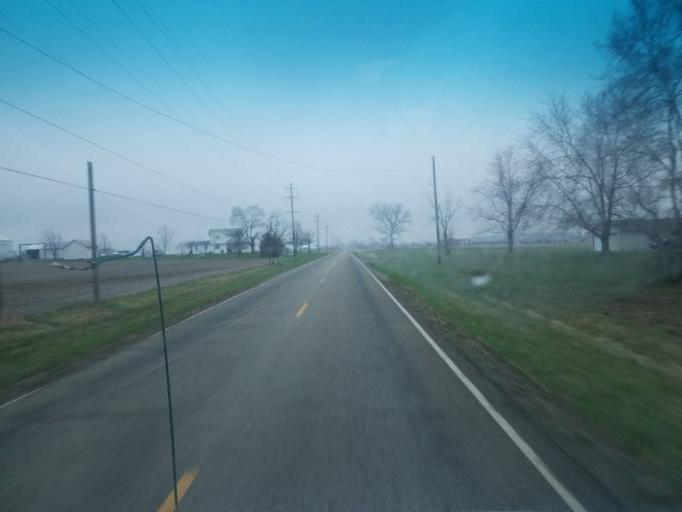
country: US
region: Ohio
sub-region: Defiance County
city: Hicksville
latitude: 41.3512
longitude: -84.7671
